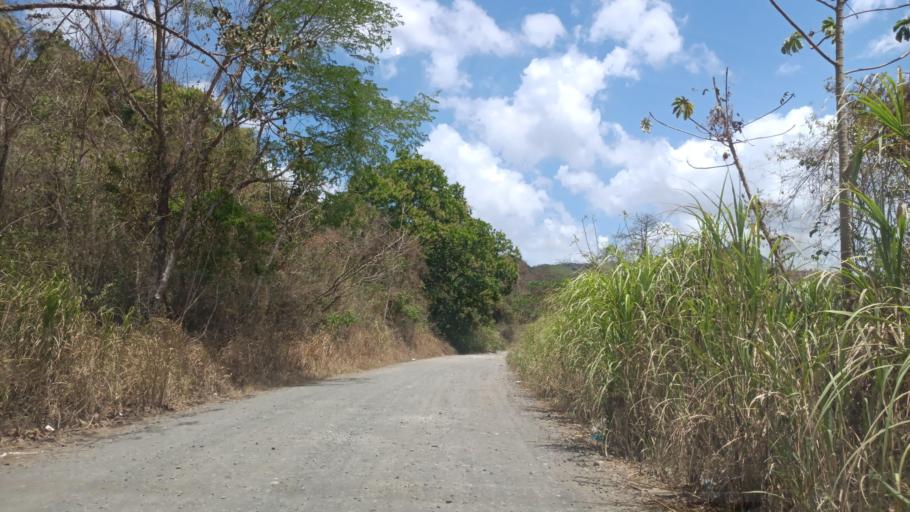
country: PA
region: Panama
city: Las Cumbres
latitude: 9.0580
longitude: -79.5680
